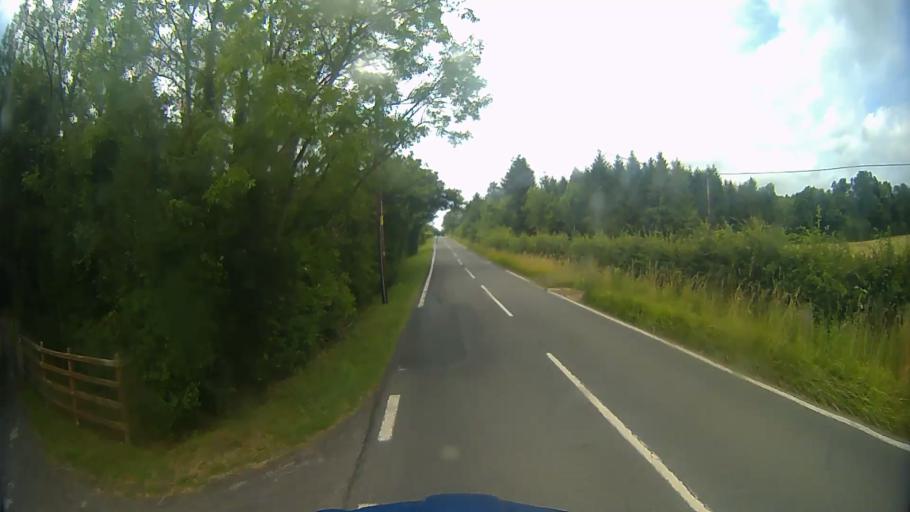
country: GB
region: England
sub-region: Hampshire
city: Kingsley
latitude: 51.1703
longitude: -0.8623
